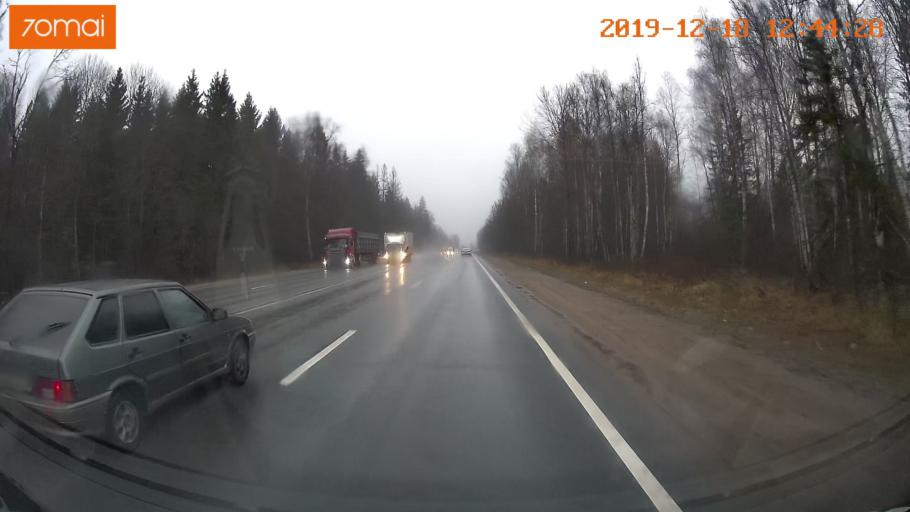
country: RU
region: Moskovskaya
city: Vysokovsk
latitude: 56.2198
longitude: 36.6489
